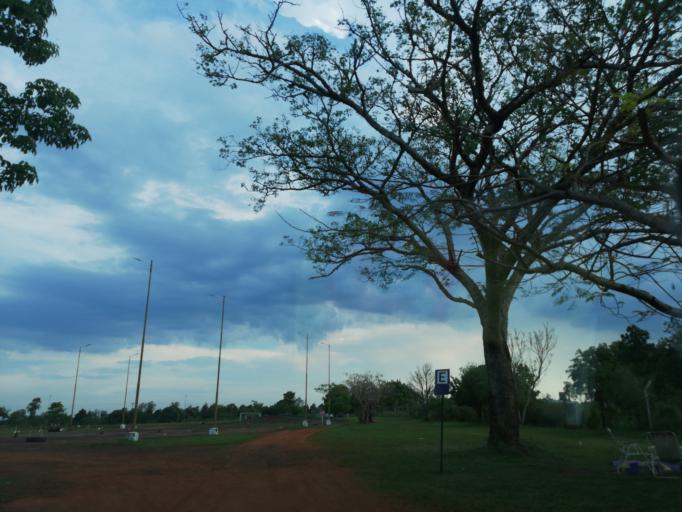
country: AR
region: Misiones
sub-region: Departamento de Capital
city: Posadas
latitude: -27.4041
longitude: -55.9731
